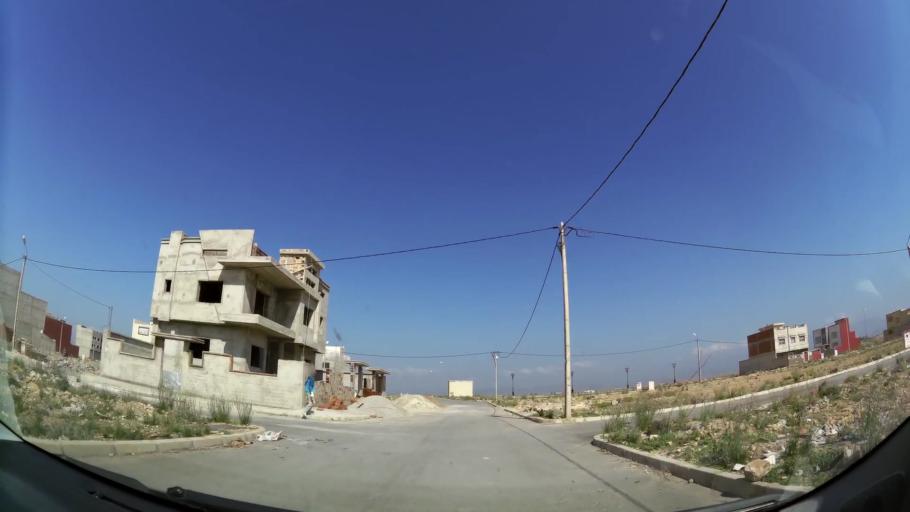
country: MA
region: Oriental
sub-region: Oujda-Angad
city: Oujda
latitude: 34.6966
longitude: -1.8683
